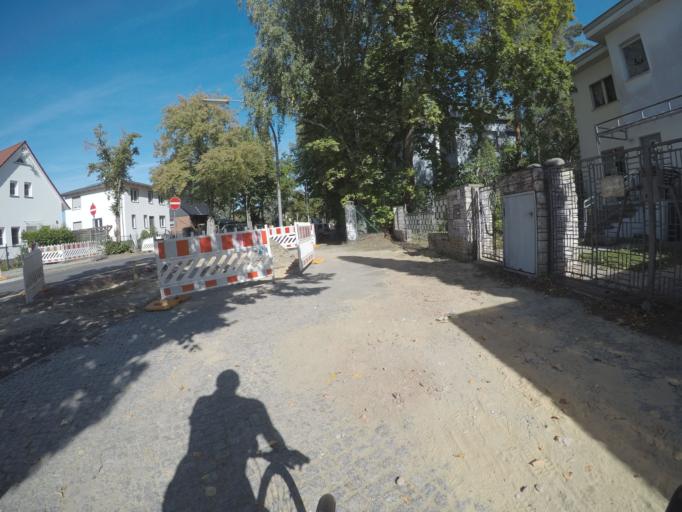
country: DE
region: Berlin
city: Heiligensee
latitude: 52.6221
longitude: 13.2243
